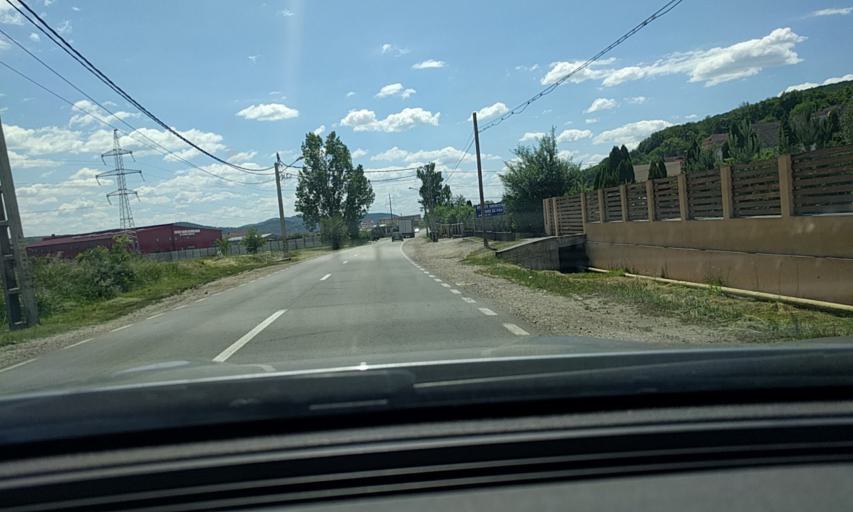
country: RO
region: Bistrita-Nasaud
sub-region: Municipiul Bistrita
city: Viisoara
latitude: 47.1170
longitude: 24.4586
